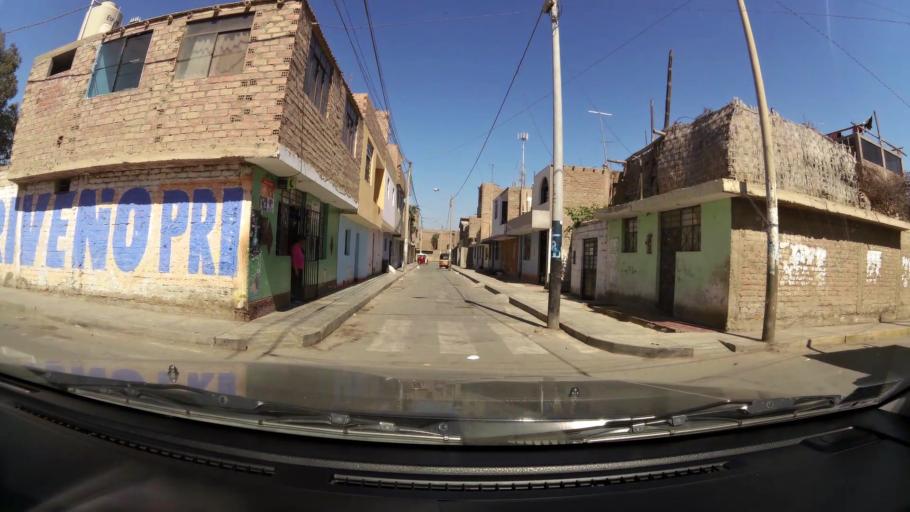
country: PE
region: Ica
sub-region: Provincia de Ica
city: Ica
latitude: -14.0577
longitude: -75.7234
